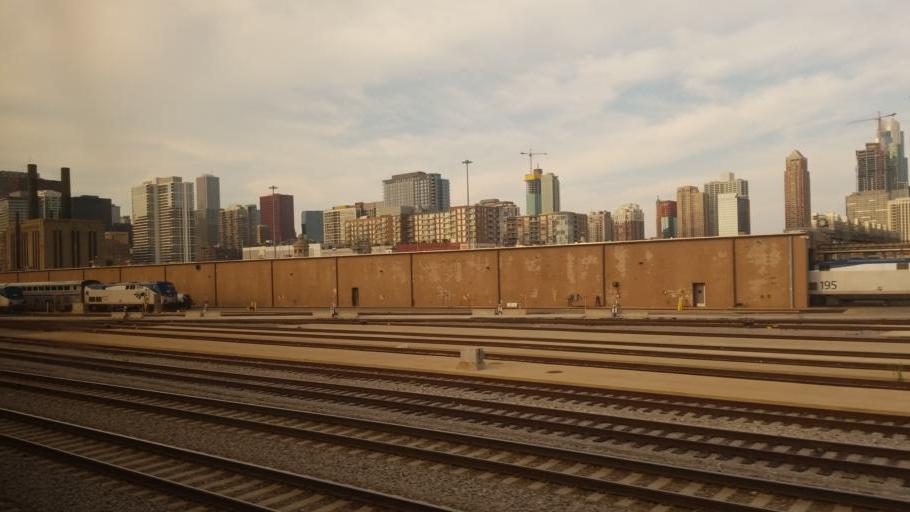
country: US
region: Illinois
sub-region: Cook County
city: Chicago
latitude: 41.8651
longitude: -87.6372
